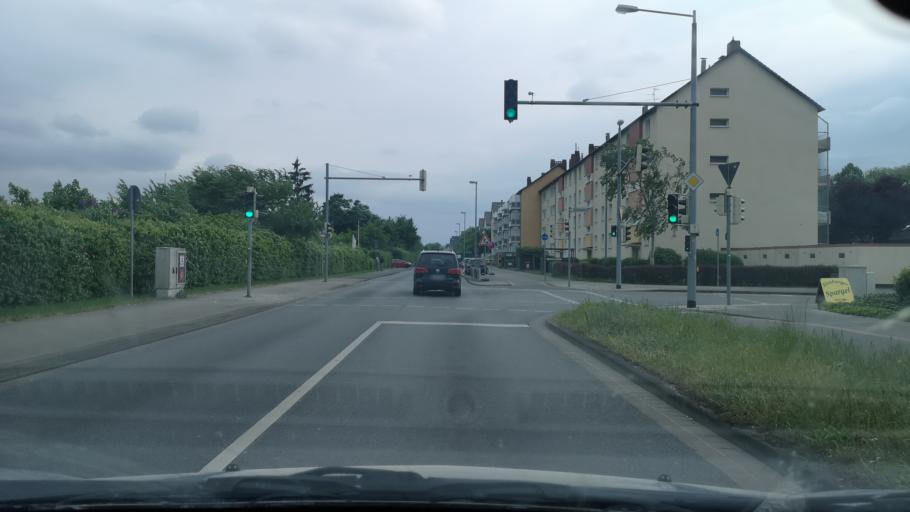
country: DE
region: Lower Saxony
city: Hannover
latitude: 52.4091
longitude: 9.6958
